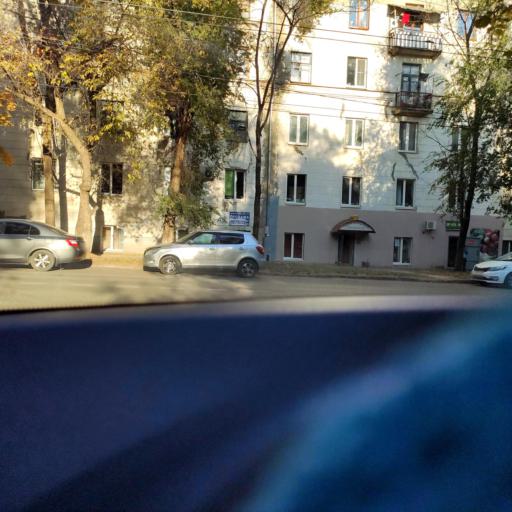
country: RU
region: Samara
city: Samara
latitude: 53.2127
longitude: 50.2409
